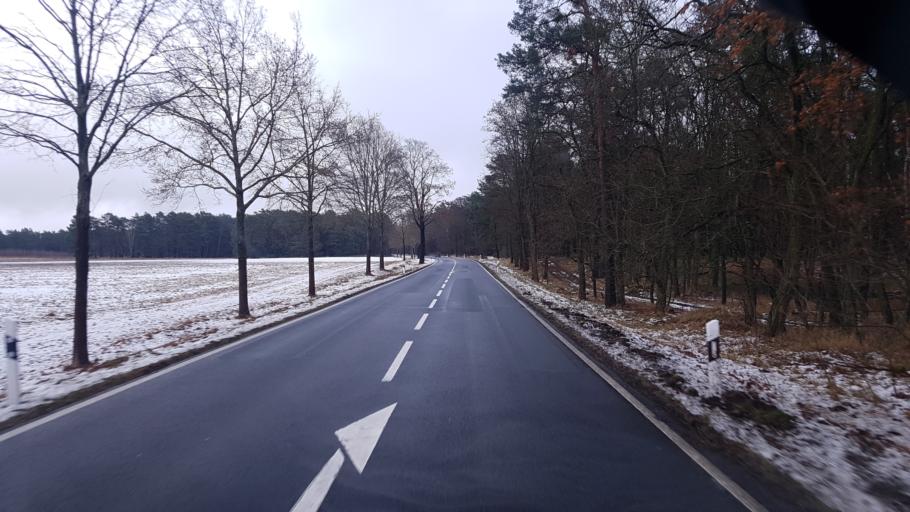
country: DE
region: Brandenburg
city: Jamlitz
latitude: 51.9844
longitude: 14.4190
